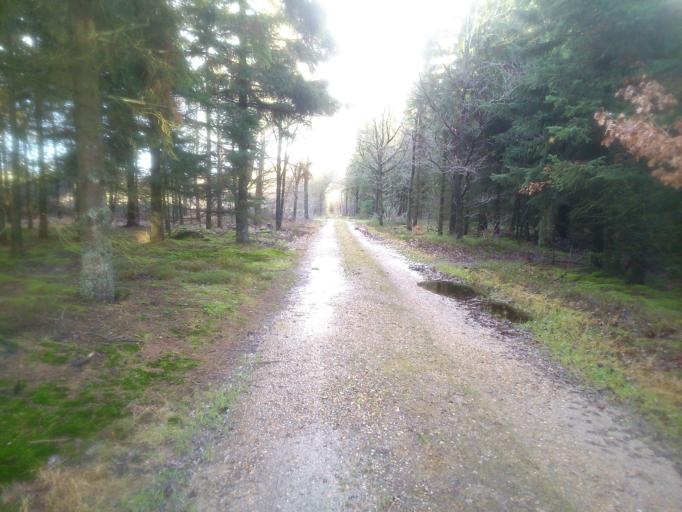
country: DK
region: Central Jutland
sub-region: Ringkobing-Skjern Kommune
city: Skjern
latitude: 55.9920
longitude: 8.4541
